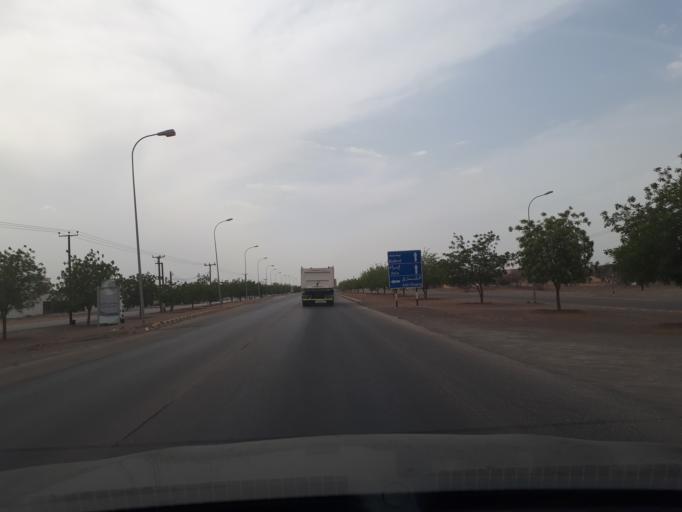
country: OM
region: Ash Sharqiyah
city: Badiyah
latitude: 22.4598
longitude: 58.8000
